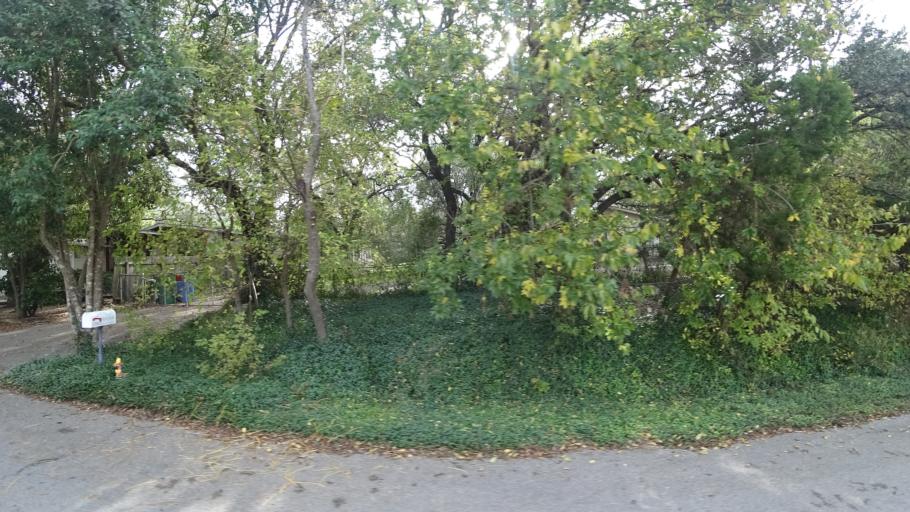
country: US
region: Texas
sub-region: Travis County
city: Hudson Bend
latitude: 30.3808
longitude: -97.9041
